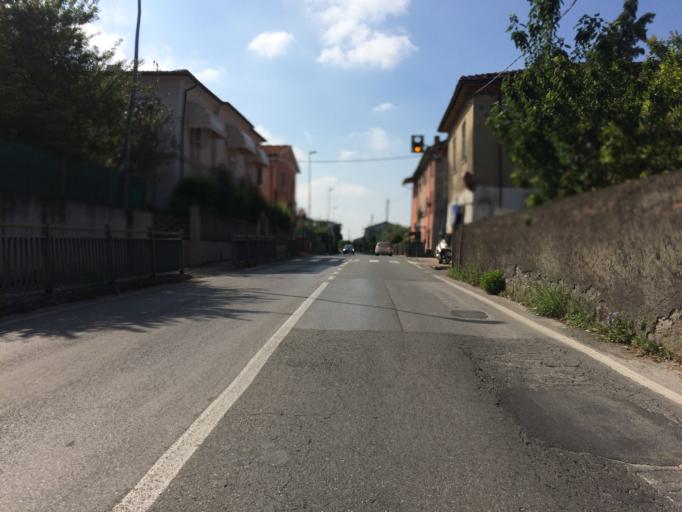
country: IT
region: Tuscany
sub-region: Provincia di Massa-Carrara
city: San Vito-Cerreto
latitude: 44.0208
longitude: 10.1493
